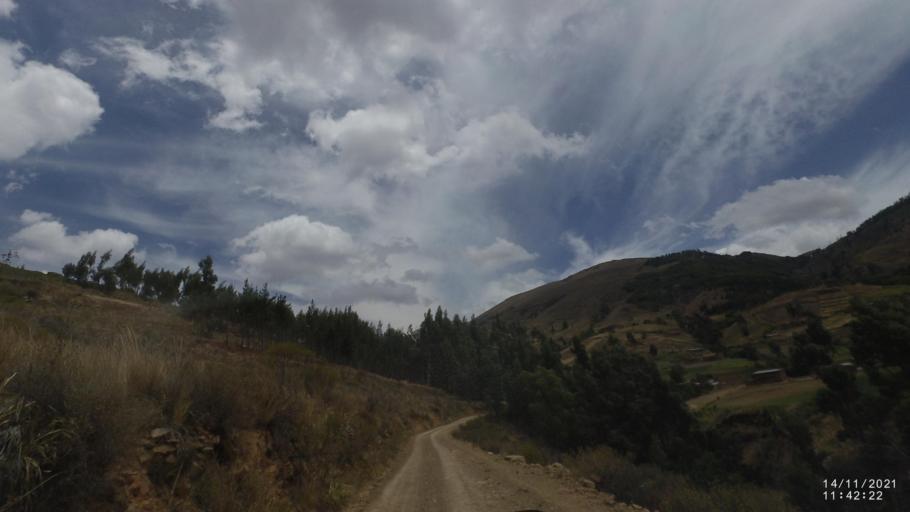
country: BO
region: Cochabamba
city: Colomi
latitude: -17.3544
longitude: -65.9908
